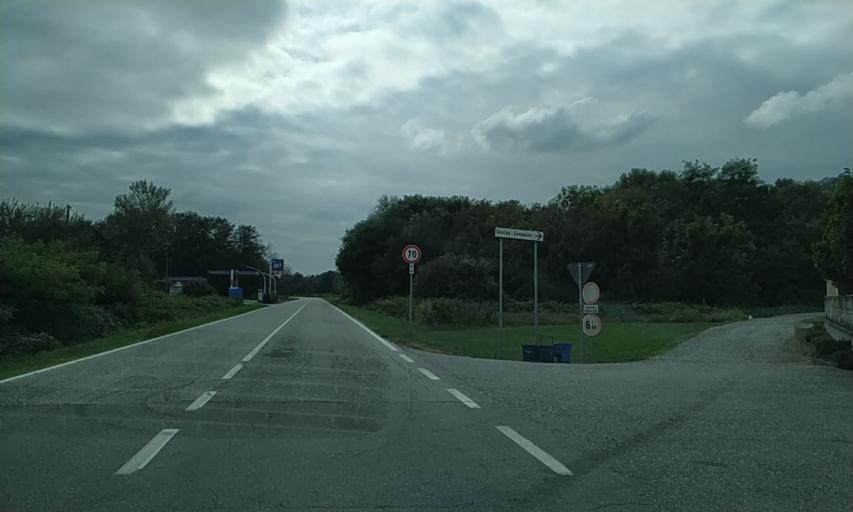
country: IT
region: Piedmont
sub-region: Provincia di Vercelli
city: Lenta
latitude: 45.5607
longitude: 8.3812
